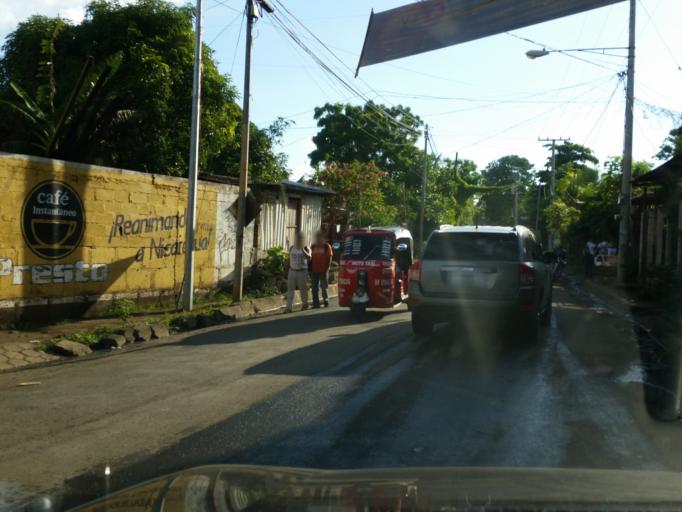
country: NI
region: Masaya
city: Ticuantepe
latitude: 12.0764
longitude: -86.2134
